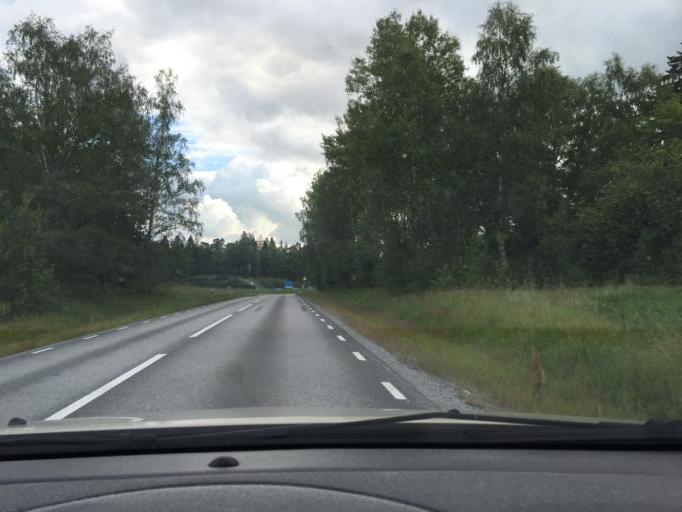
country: SE
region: Stockholm
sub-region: Salems Kommun
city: Ronninge
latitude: 59.2162
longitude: 17.7593
